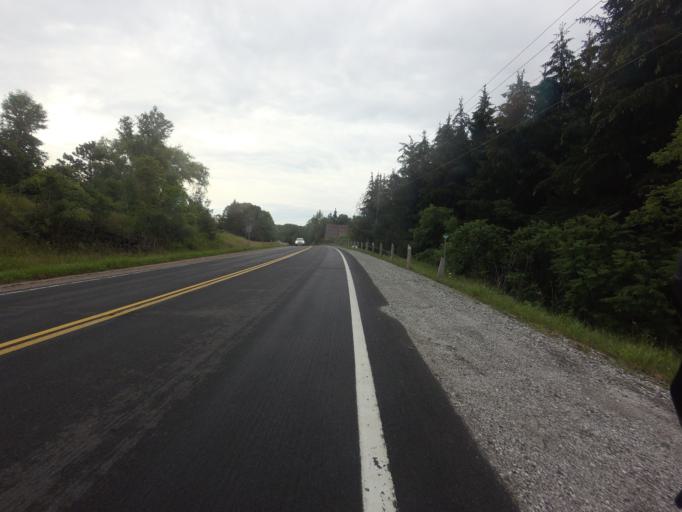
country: CA
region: Ontario
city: Perth
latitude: 45.0358
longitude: -76.3903
